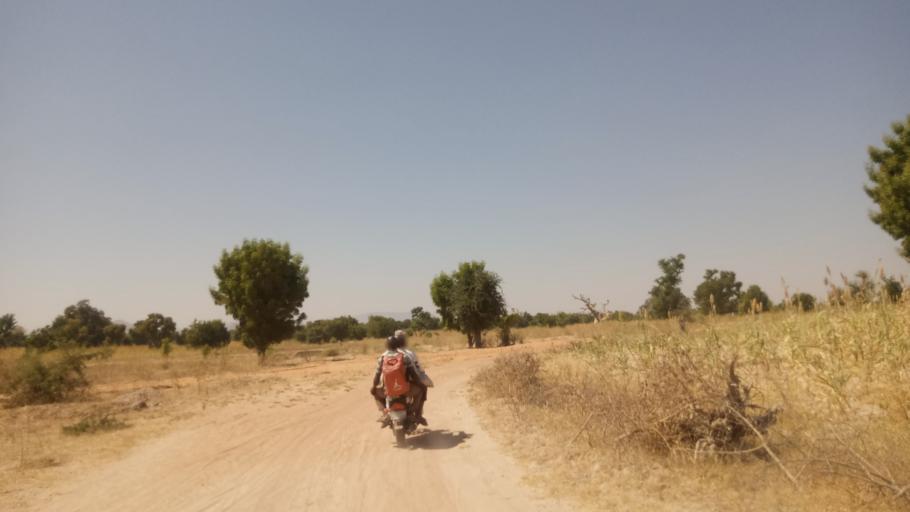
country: NG
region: Adamawa
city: Mayo Belwa
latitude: 9.0866
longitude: 12.0273
